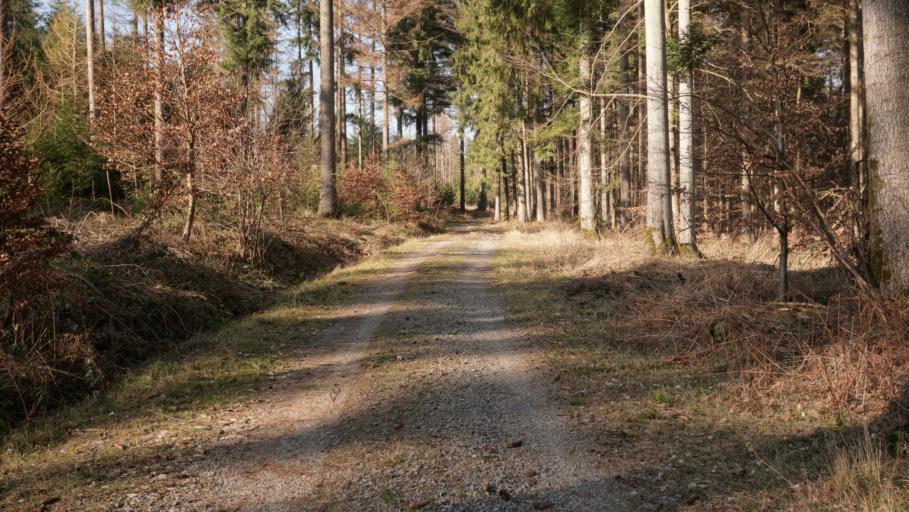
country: DE
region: Baden-Wuerttemberg
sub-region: Karlsruhe Region
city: Fahrenbach
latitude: 49.4461
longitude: 9.1470
